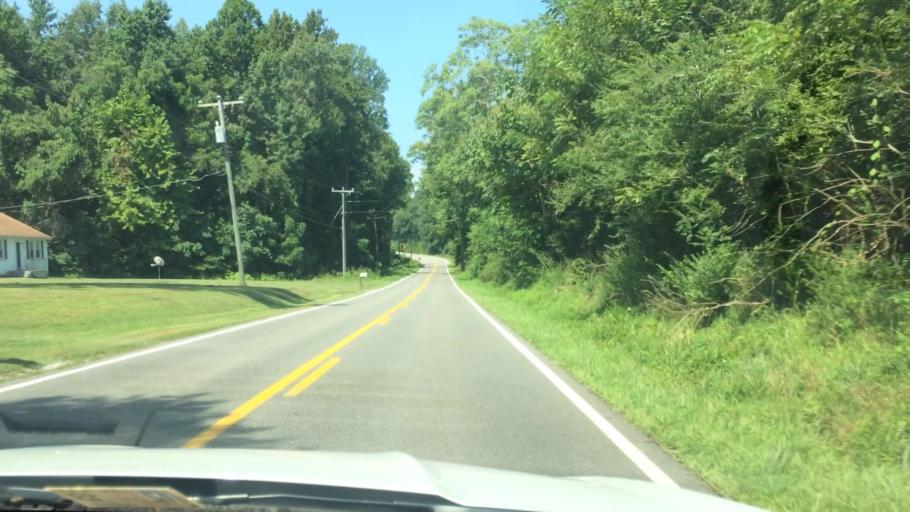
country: US
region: Virginia
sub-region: New Kent County
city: New Kent
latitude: 37.5241
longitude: -77.0685
